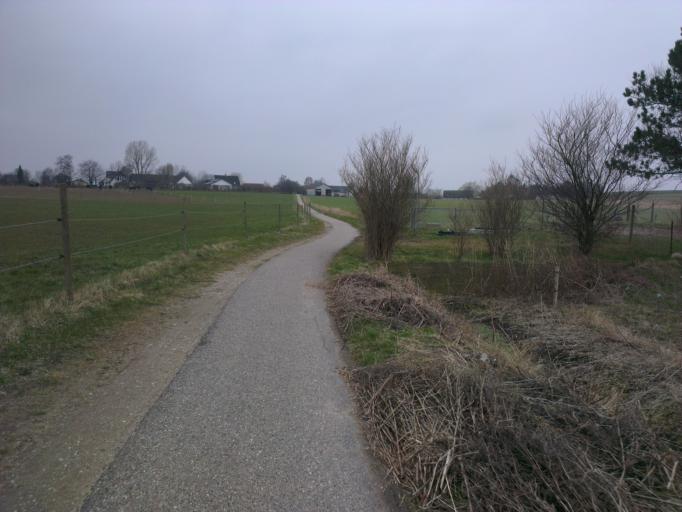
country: DK
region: Capital Region
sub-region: Frederikssund Kommune
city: Slangerup
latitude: 55.8506
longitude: 12.1383
